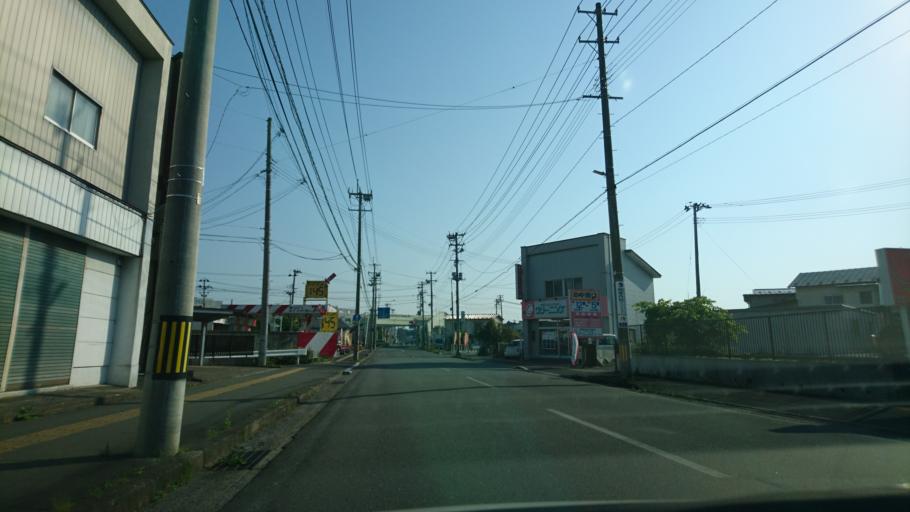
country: JP
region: Iwate
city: Ichinoseki
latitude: 38.9320
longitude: 141.1234
